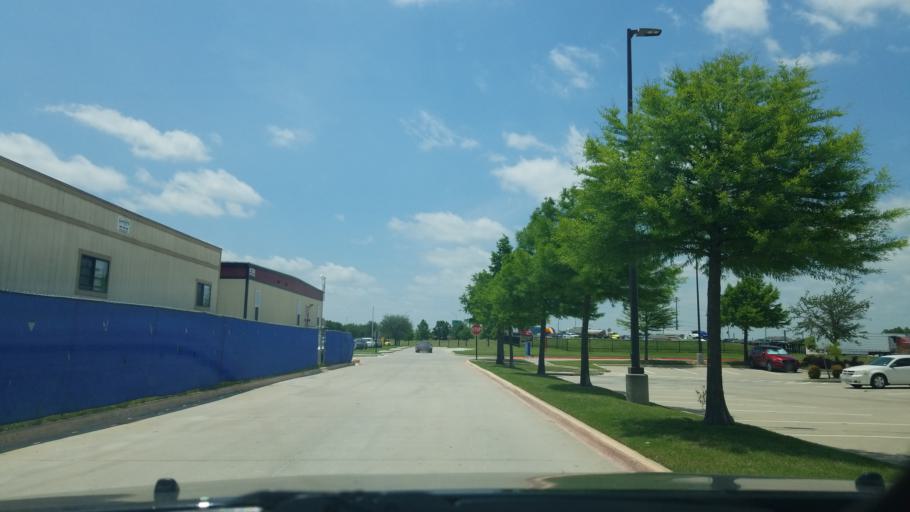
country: US
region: Texas
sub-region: Denton County
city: Denton
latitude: 33.2186
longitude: -97.1686
